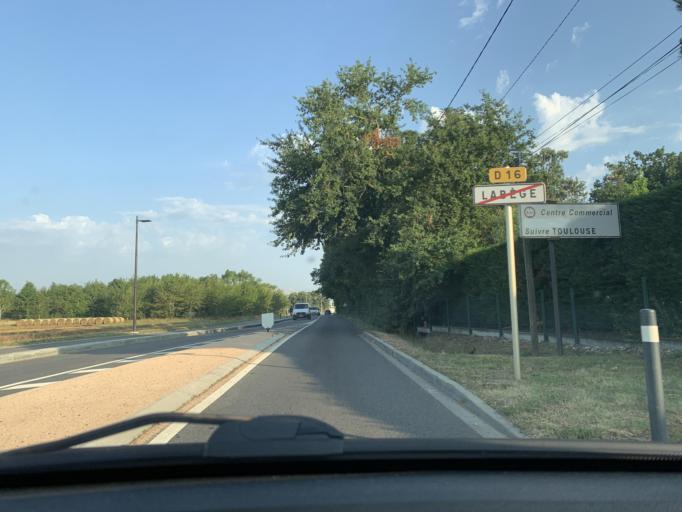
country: FR
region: Midi-Pyrenees
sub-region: Departement de la Haute-Garonne
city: Labege
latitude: 43.5351
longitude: 1.5304
